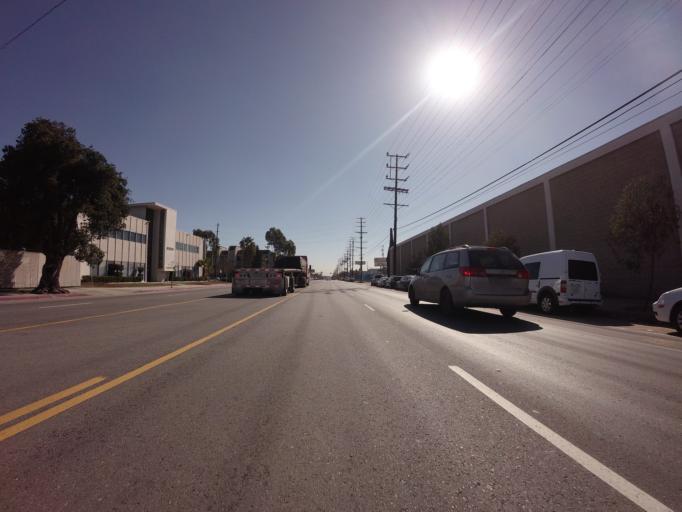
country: US
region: California
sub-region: Los Angeles County
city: North Hollywood
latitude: 34.2364
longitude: -118.3735
